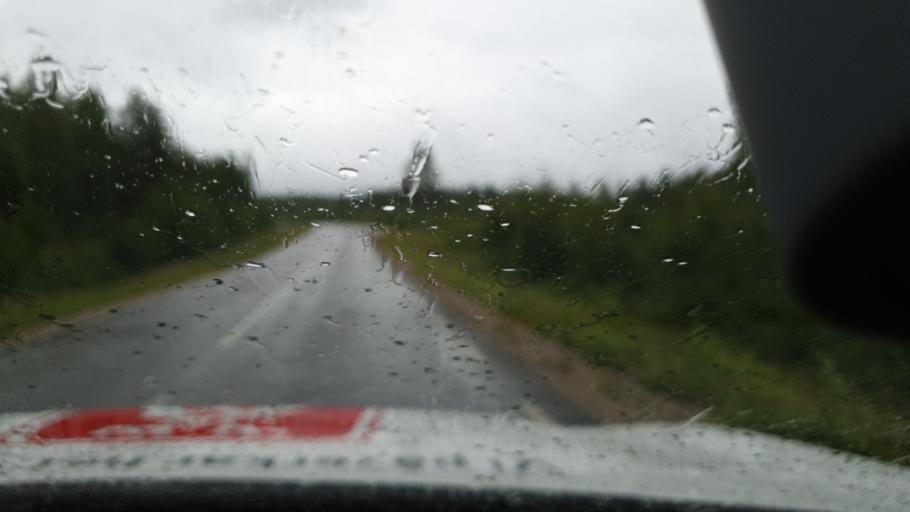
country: SE
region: Vaesterbotten
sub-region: Vindelns Kommun
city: Vindeln
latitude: 64.5380
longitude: 19.9008
